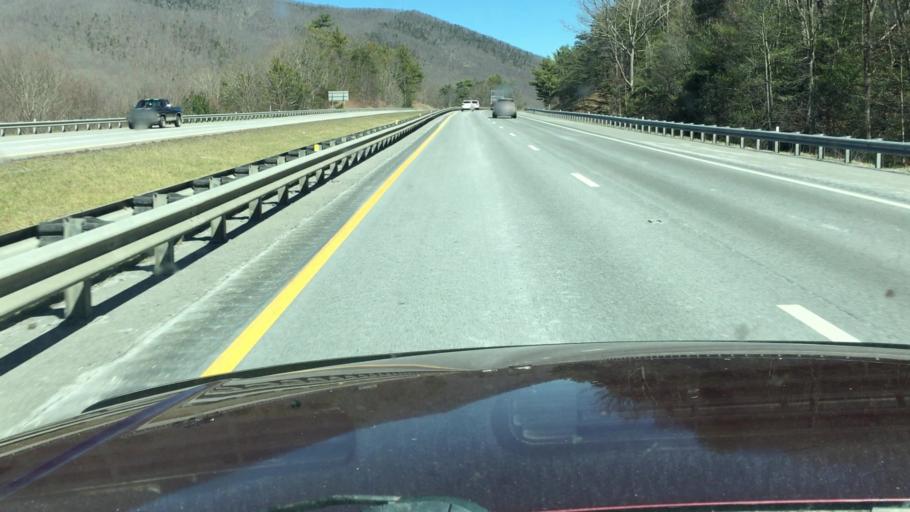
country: US
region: Virginia
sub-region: Bland County
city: Bland
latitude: 37.1979
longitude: -81.1102
